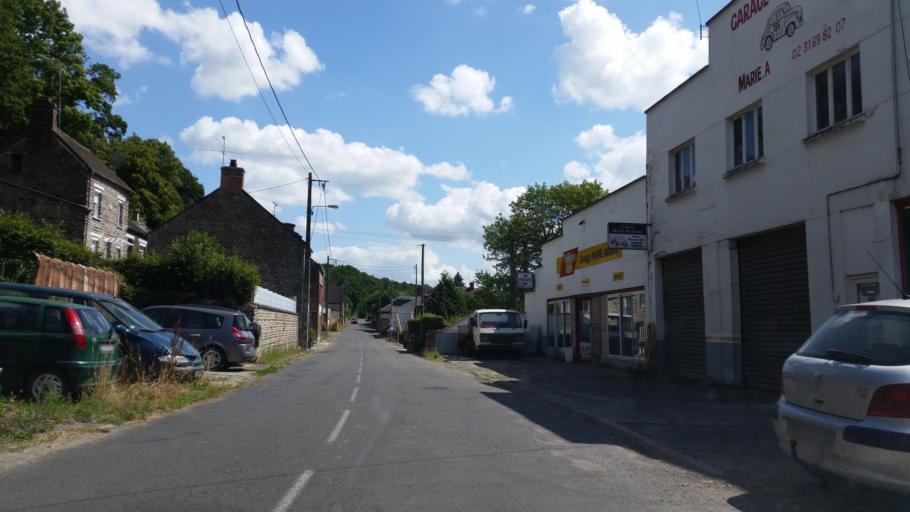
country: FR
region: Lower Normandy
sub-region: Departement du Calvados
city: Clecy
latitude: 48.8575
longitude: -0.3978
